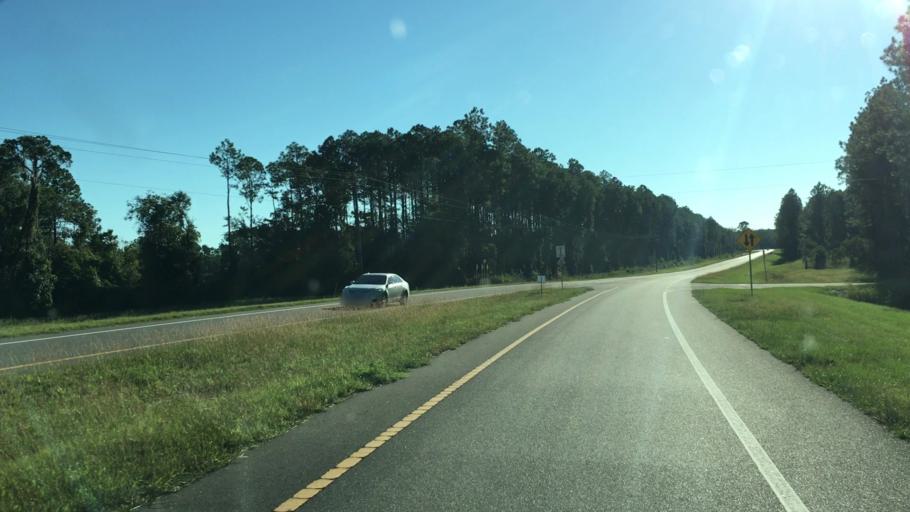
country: US
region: Florida
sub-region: Alachua County
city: Waldo
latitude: 29.7162
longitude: -82.1298
